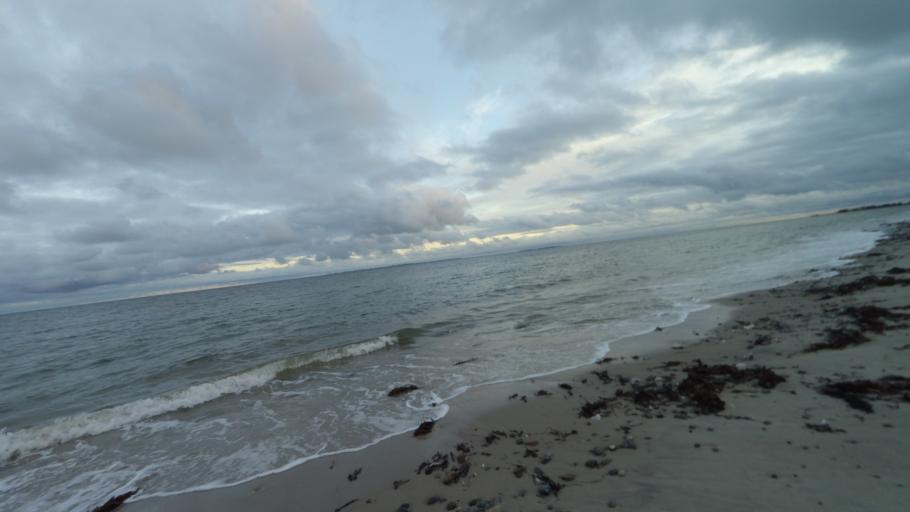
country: DK
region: Central Jutland
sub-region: Arhus Kommune
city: Beder
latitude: 56.0433
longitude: 10.2709
